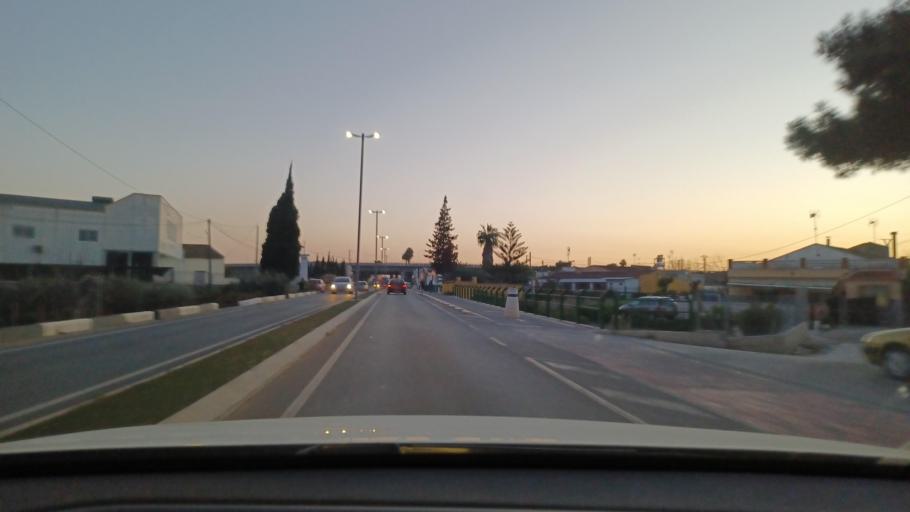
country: ES
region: Valencia
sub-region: Provincia de Alicante
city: Dolores
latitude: 38.1276
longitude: -0.7788
